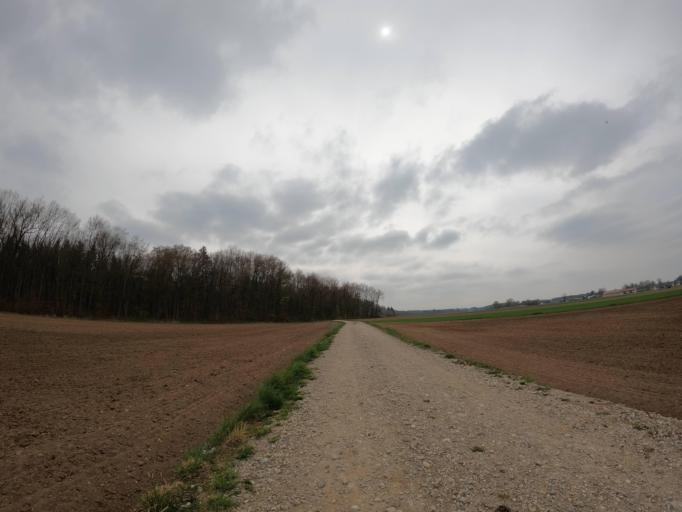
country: DE
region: Bavaria
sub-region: Upper Bavaria
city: Anzing
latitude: 48.1322
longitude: 11.8452
